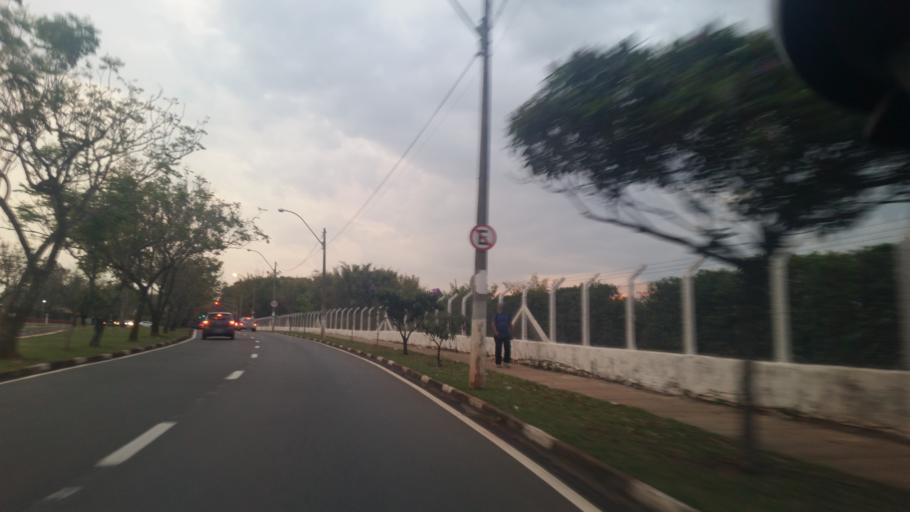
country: BR
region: Sao Paulo
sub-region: Campinas
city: Campinas
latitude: -22.8719
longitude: -47.0660
